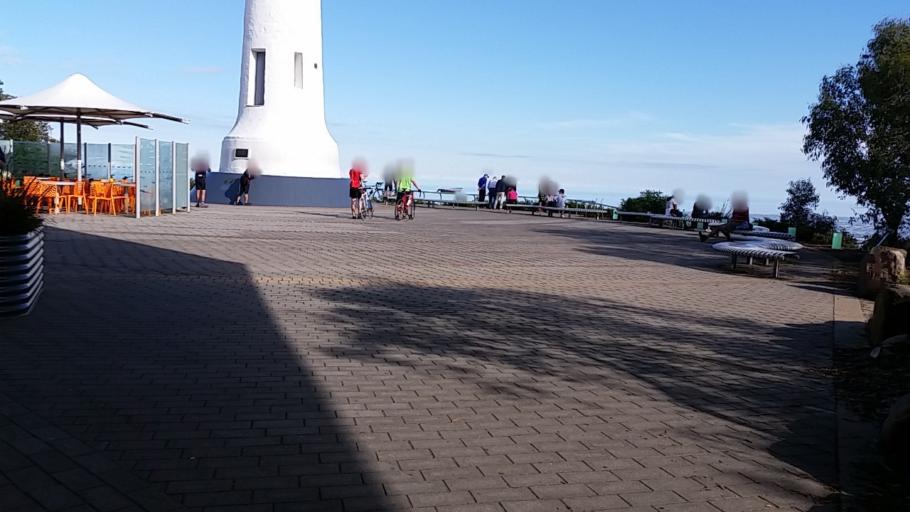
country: AU
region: South Australia
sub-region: Adelaide Hills
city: Crafers
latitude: -34.9741
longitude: 138.7093
